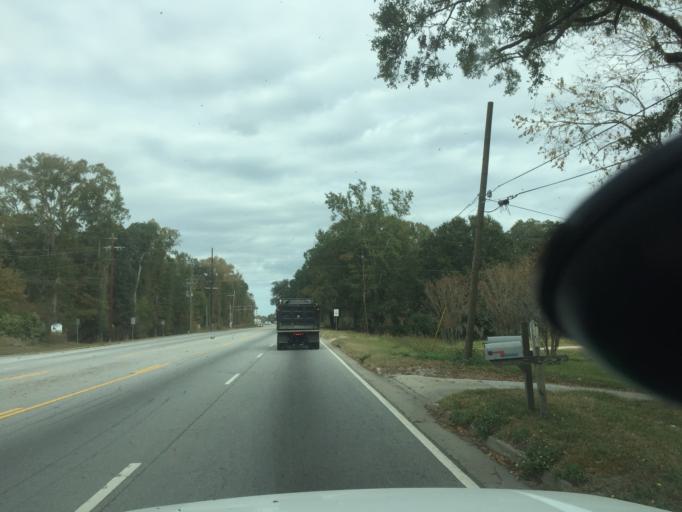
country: US
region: Georgia
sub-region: Chatham County
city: Garden City
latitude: 32.0998
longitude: -81.1960
